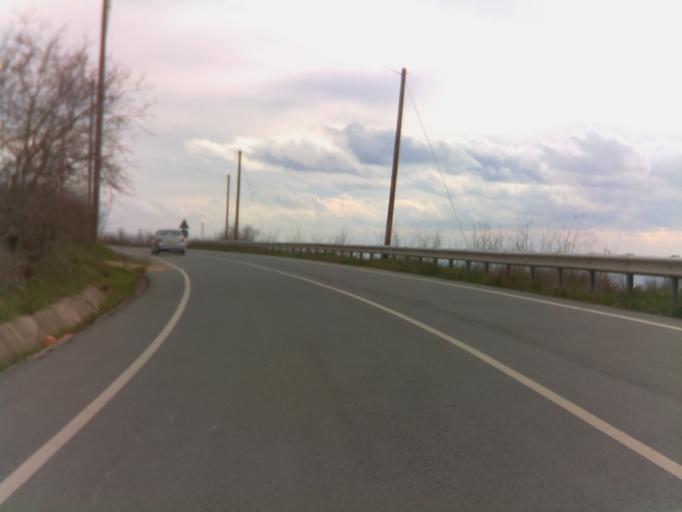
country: CY
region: Pafos
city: Pegeia
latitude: 34.9181
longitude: 32.4203
